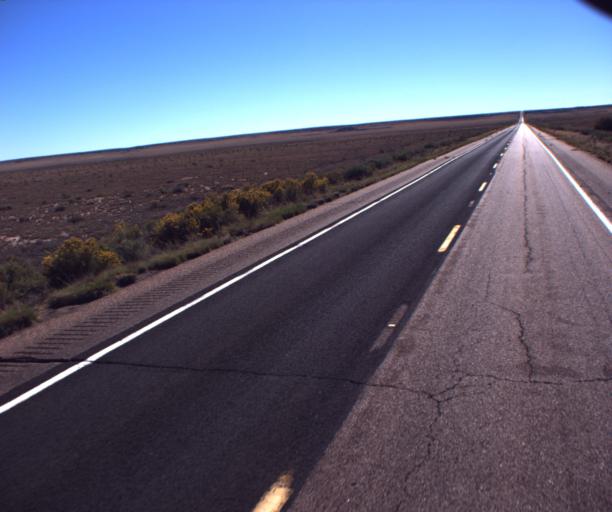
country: US
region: Arizona
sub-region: Navajo County
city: Snowflake
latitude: 34.7428
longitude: -109.7942
